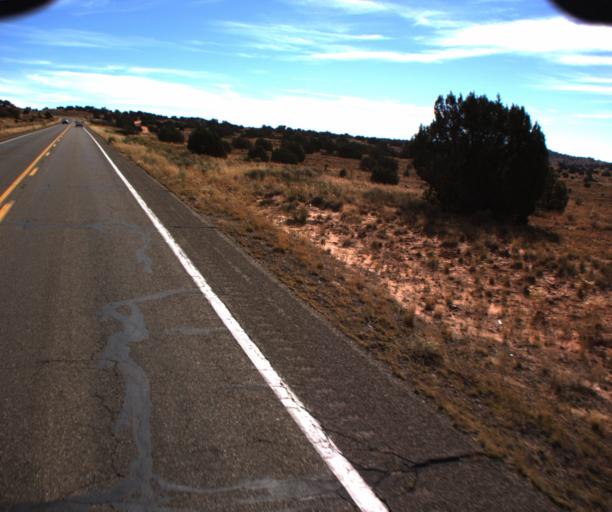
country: US
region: Arizona
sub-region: Coconino County
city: Kaibito
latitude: 36.5770
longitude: -111.1269
